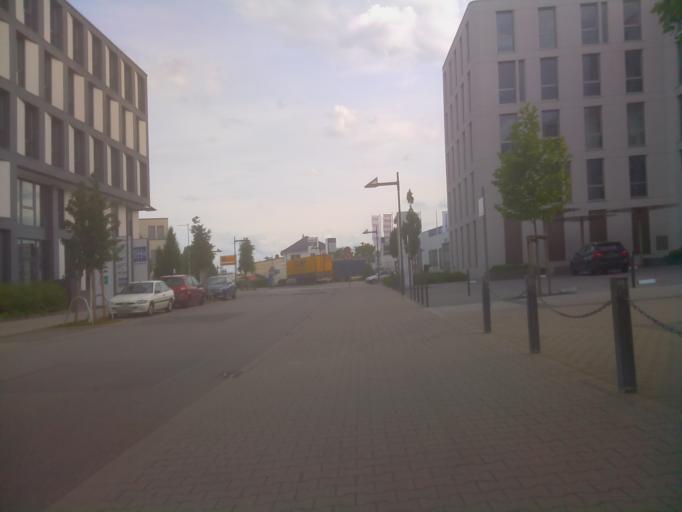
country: DE
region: Baden-Wuerttemberg
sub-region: Karlsruhe Region
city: Mannheim
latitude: 49.4770
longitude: 8.5054
